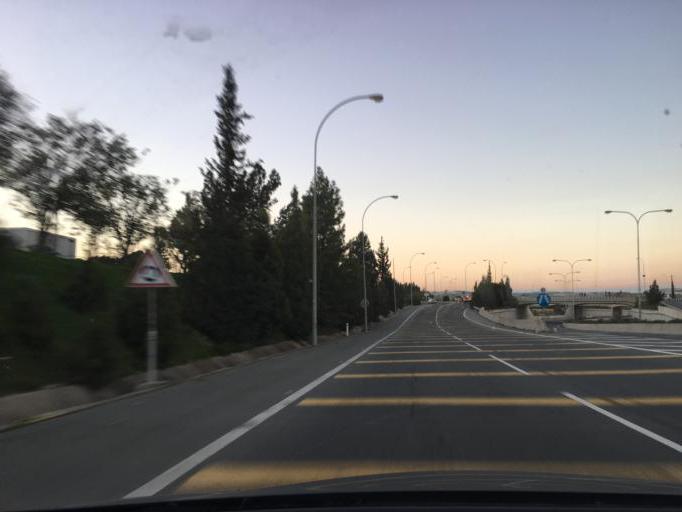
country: CY
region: Larnaka
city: Dhromolaxia
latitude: 34.9059
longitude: 33.5685
